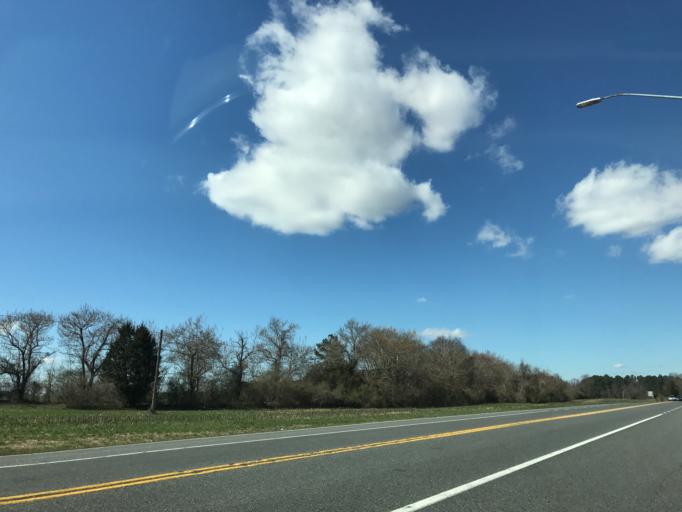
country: US
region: Maryland
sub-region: Queen Anne's County
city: Kingstown
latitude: 39.1546
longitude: -75.9815
